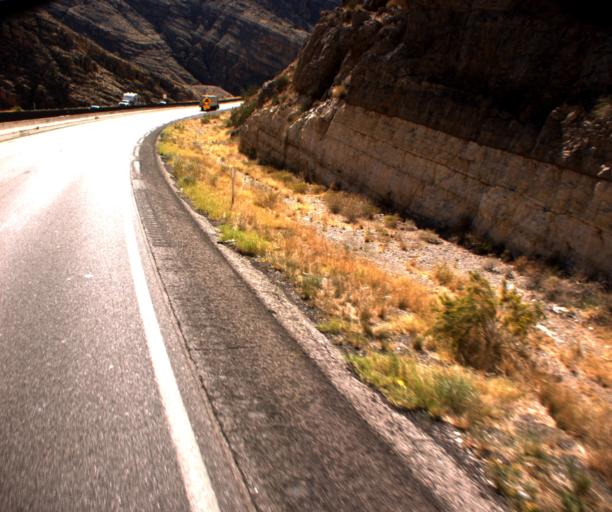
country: US
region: Arizona
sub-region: Mohave County
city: Beaver Dam
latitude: 36.9216
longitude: -113.8322
